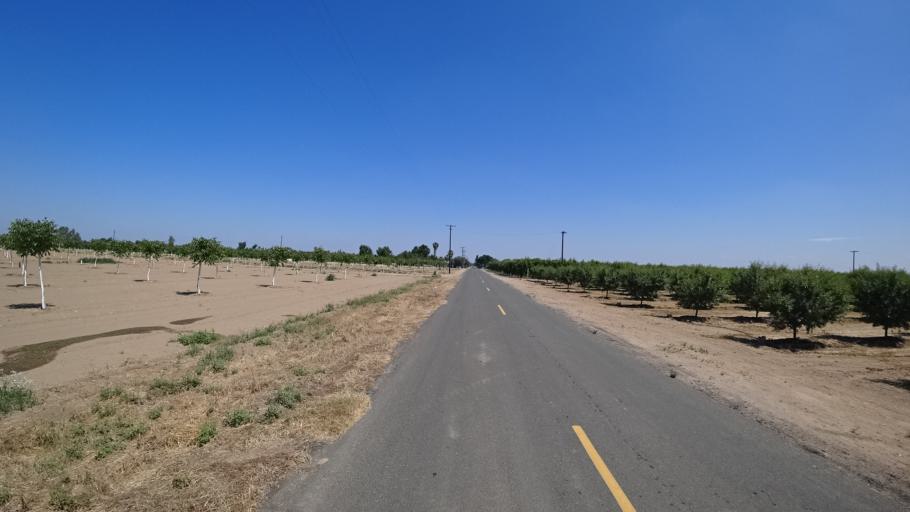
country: US
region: California
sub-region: Fresno County
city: Kingsburg
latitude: 36.4627
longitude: -119.5734
